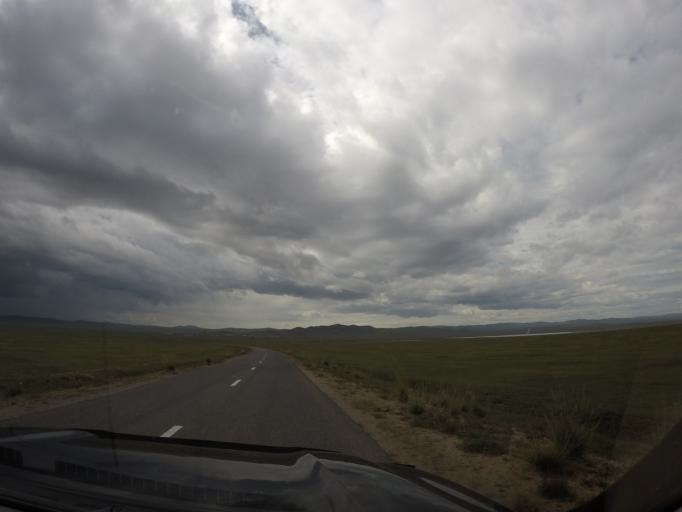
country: MN
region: Hentiy
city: Avraga
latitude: 47.4786
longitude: 109.5168
